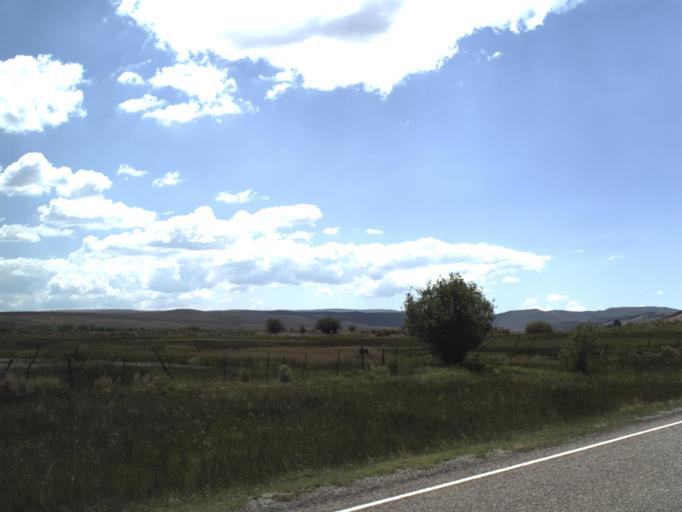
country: US
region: Utah
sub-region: Rich County
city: Randolph
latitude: 41.5241
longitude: -111.1762
